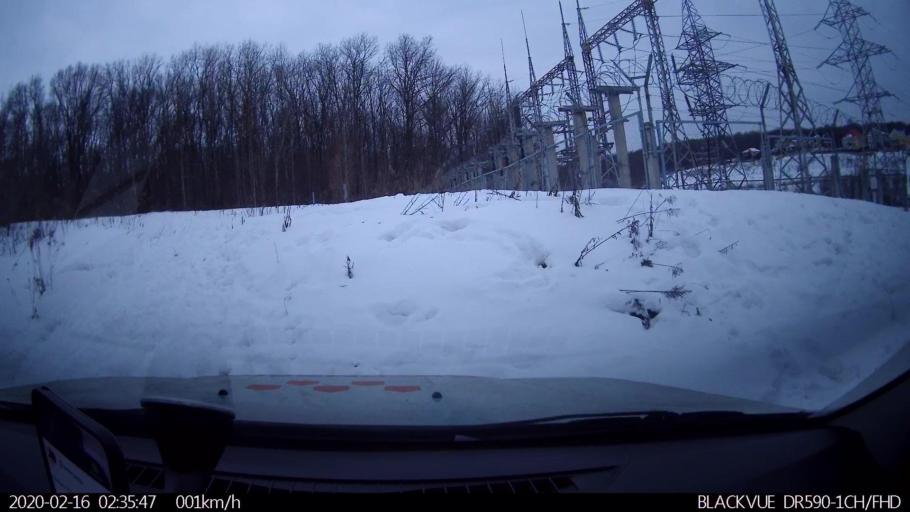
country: RU
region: Nizjnij Novgorod
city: Nizhniy Novgorod
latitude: 56.2750
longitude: 44.0263
